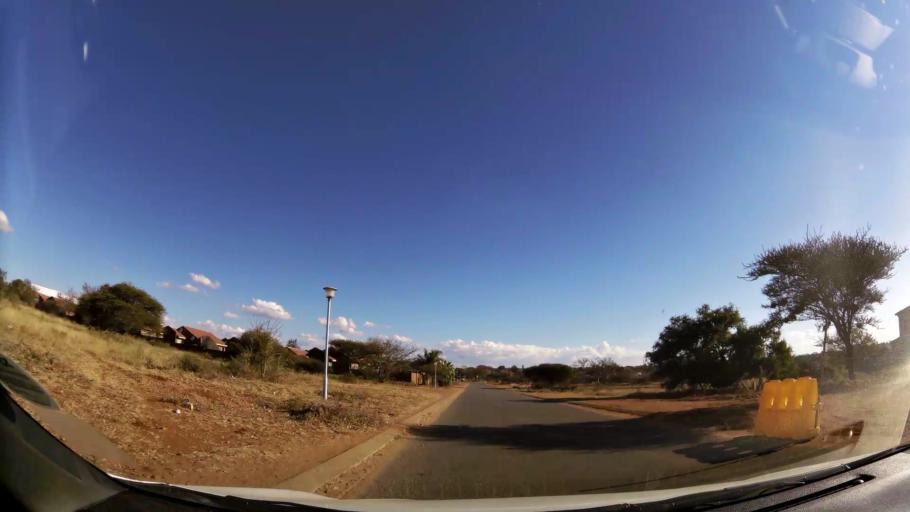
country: ZA
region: Limpopo
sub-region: Capricorn District Municipality
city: Polokwane
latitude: -23.8828
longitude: 29.4972
